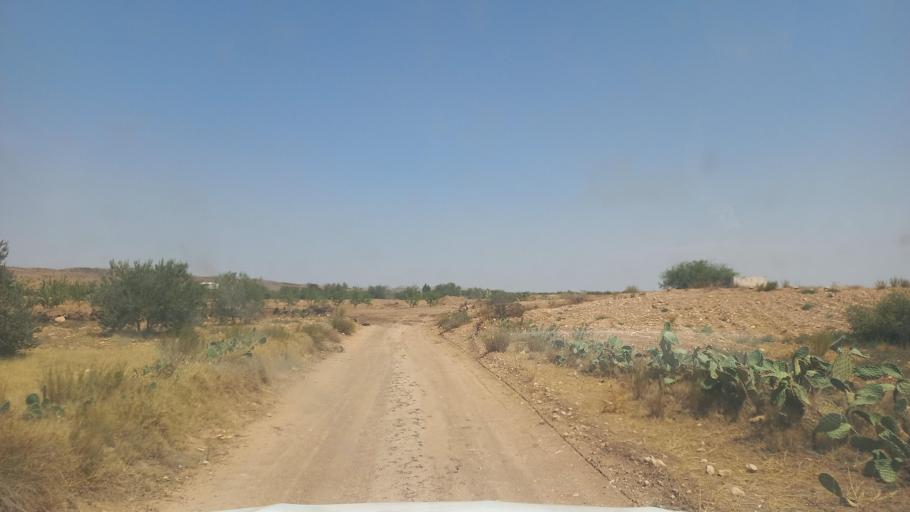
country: TN
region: Al Qasrayn
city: Kasserine
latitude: 35.2921
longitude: 8.9533
